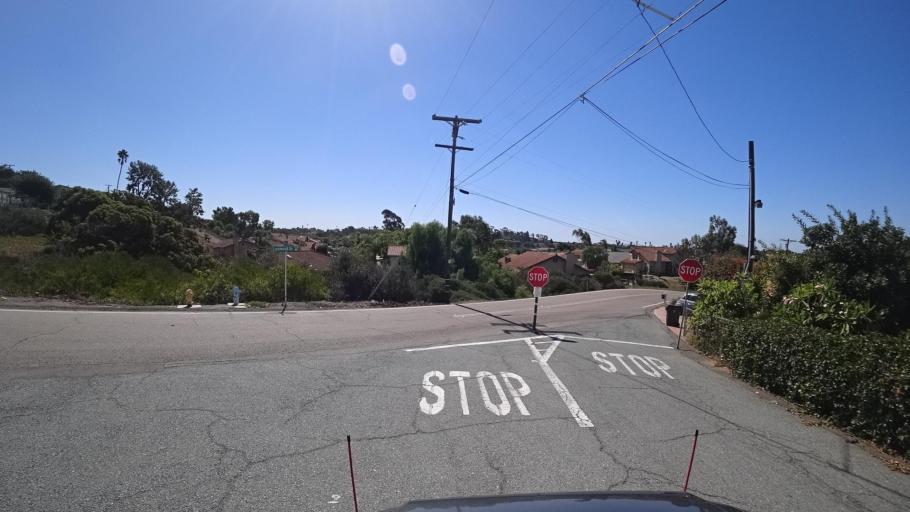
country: US
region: California
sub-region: San Diego County
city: Bonita
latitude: 32.6455
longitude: -117.0526
